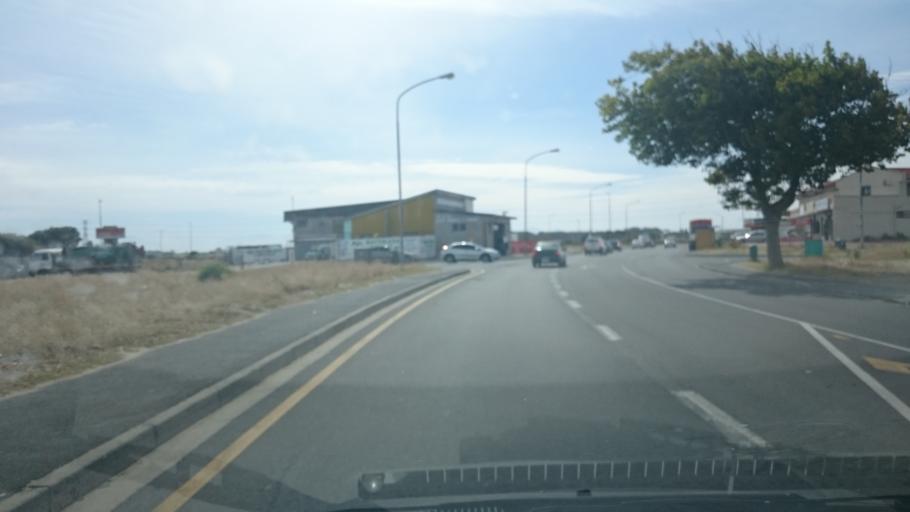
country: ZA
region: Western Cape
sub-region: City of Cape Town
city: Lansdowne
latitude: -34.0219
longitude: 18.5210
